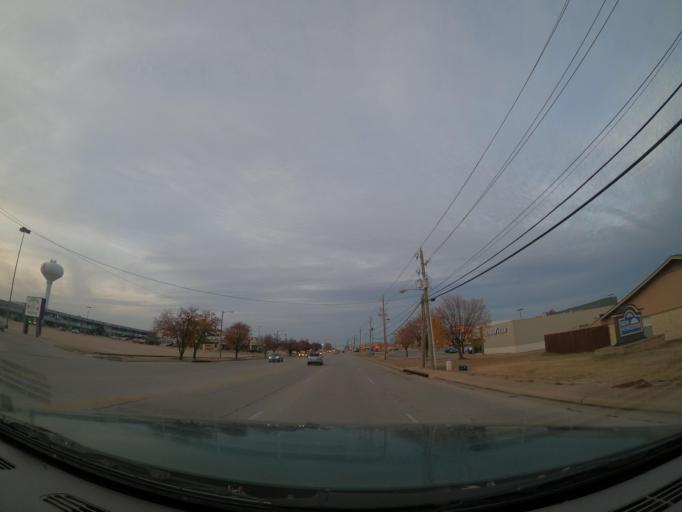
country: US
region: Oklahoma
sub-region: Tulsa County
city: Broken Arrow
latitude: 36.0144
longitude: -95.7974
